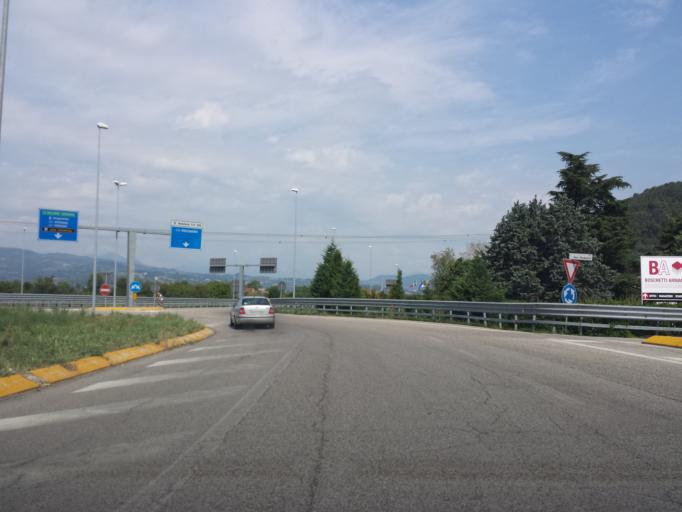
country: IT
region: Veneto
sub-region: Provincia di Vicenza
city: Tezze
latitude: 45.5187
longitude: 11.3878
